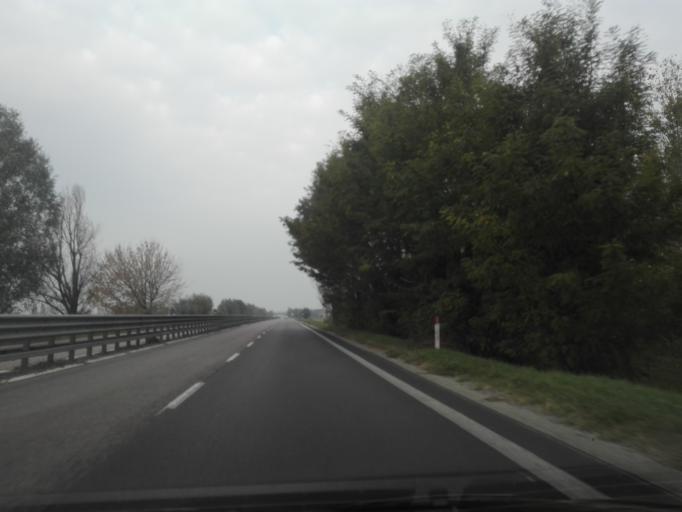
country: IT
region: Veneto
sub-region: Provincia di Verona
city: Spinimbecco
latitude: 45.1331
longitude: 11.3684
